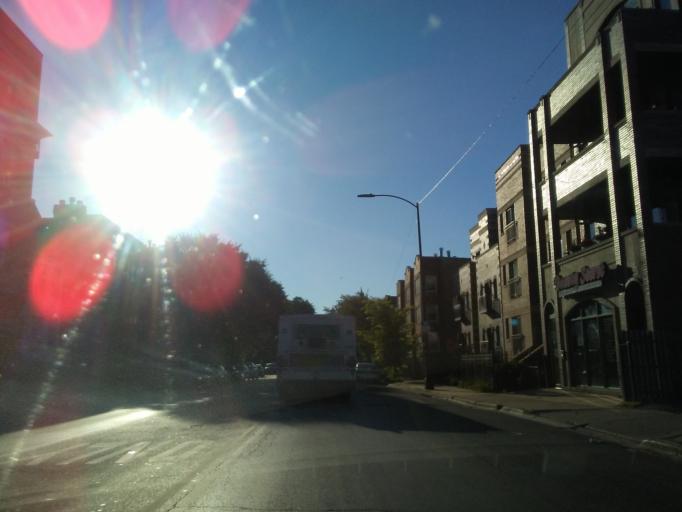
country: US
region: Illinois
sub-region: Cook County
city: Lincolnwood
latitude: 41.9758
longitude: -87.6919
